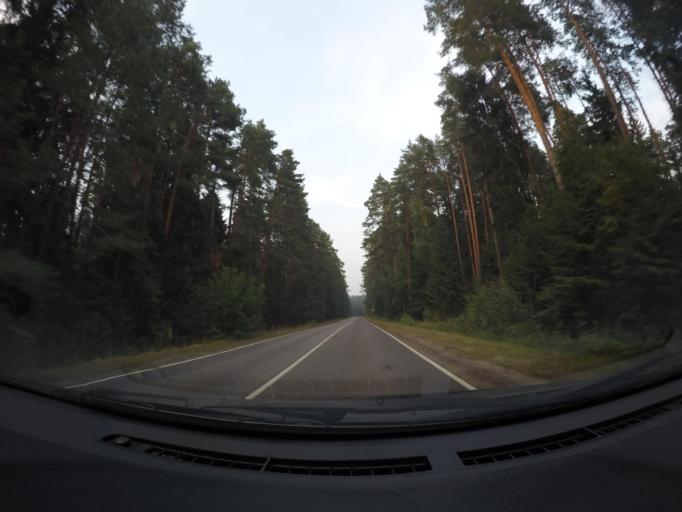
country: RU
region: Moskovskaya
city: Imeni Tsyurupy
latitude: 55.5019
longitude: 38.7059
